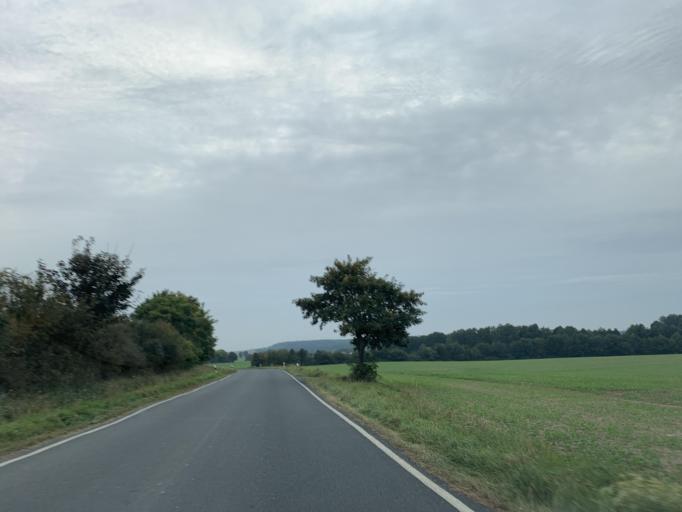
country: DE
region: Brandenburg
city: Mittenwalde
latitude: 53.3173
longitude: 13.6941
